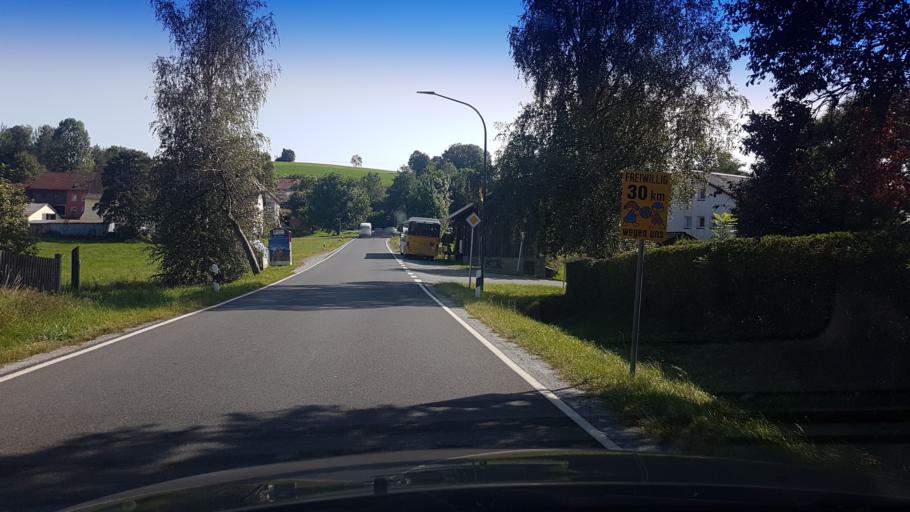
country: DE
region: Bavaria
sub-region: Upper Franconia
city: Marktschorgast
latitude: 50.0763
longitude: 11.6723
